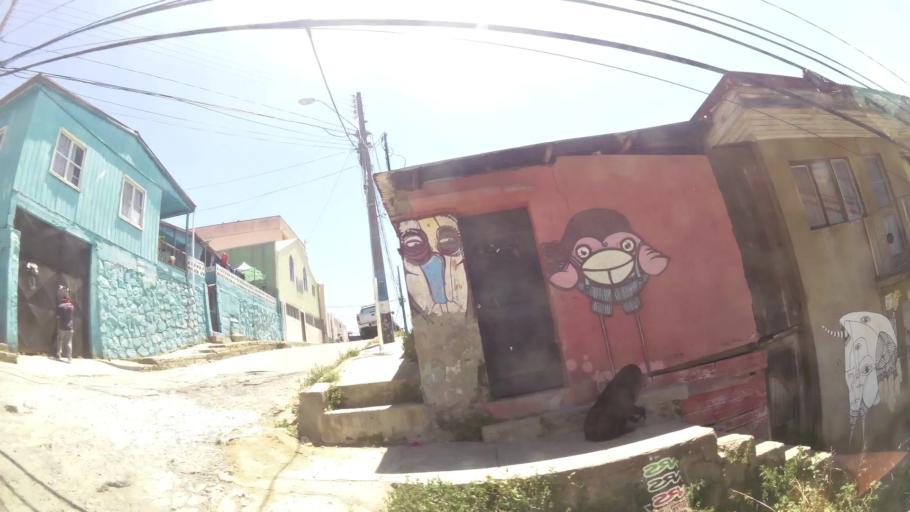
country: CL
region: Valparaiso
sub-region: Provincia de Valparaiso
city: Valparaiso
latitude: -33.0538
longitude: -71.6286
